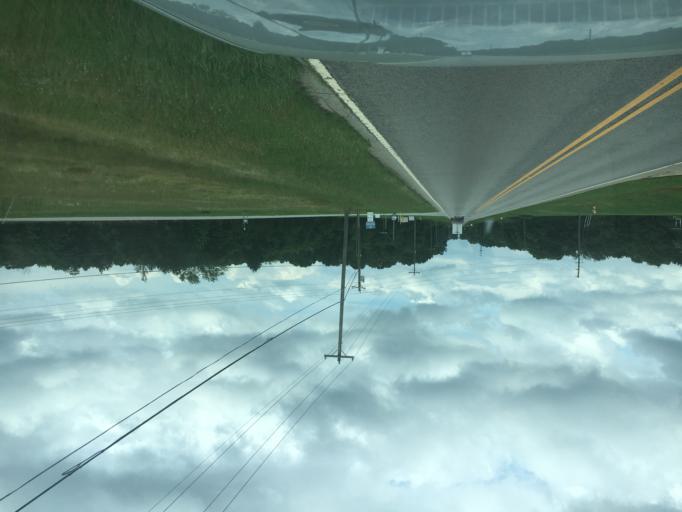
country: US
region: South Carolina
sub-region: Anderson County
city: Williamston
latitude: 34.6302
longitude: -82.3998
